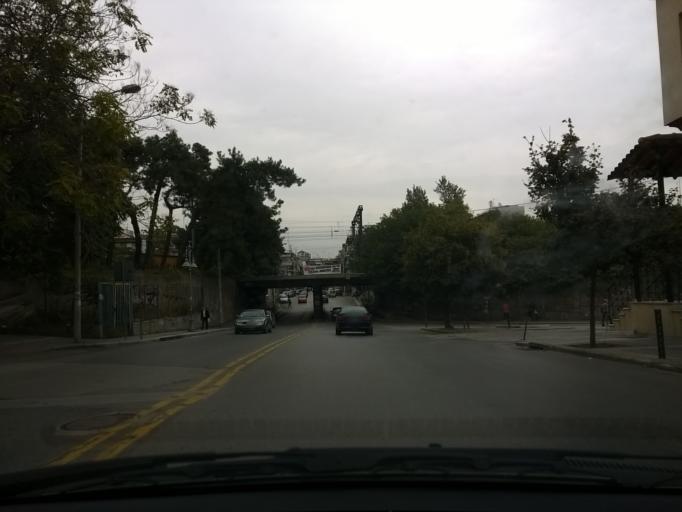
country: GR
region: Central Macedonia
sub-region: Nomos Thessalonikis
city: Thessaloniki
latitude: 40.6461
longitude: 22.9260
